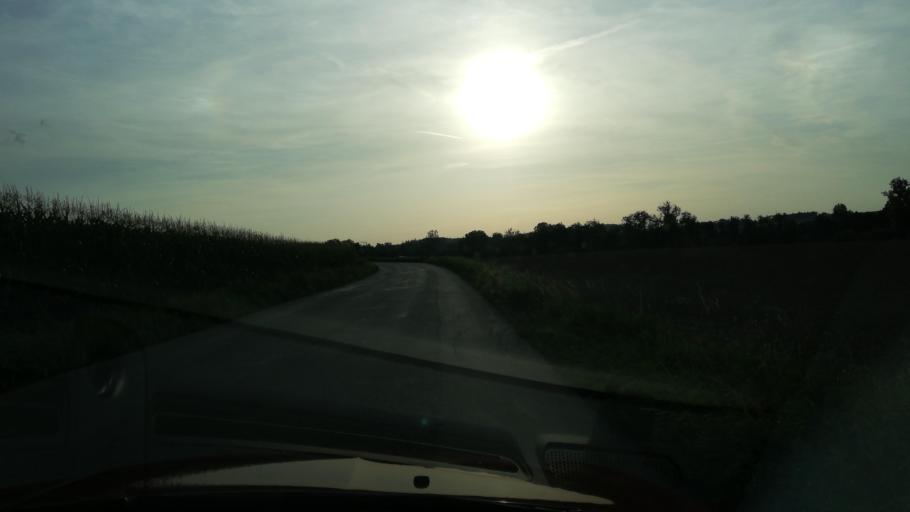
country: AT
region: Upper Austria
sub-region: Wels-Land
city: Gunskirchen
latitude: 48.1315
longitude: 13.9292
